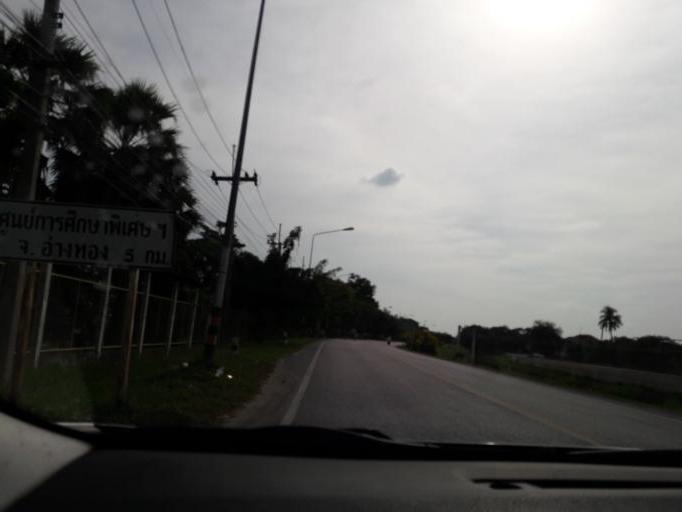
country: TH
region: Ang Thong
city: Ang Thong
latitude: 14.5899
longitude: 100.4456
